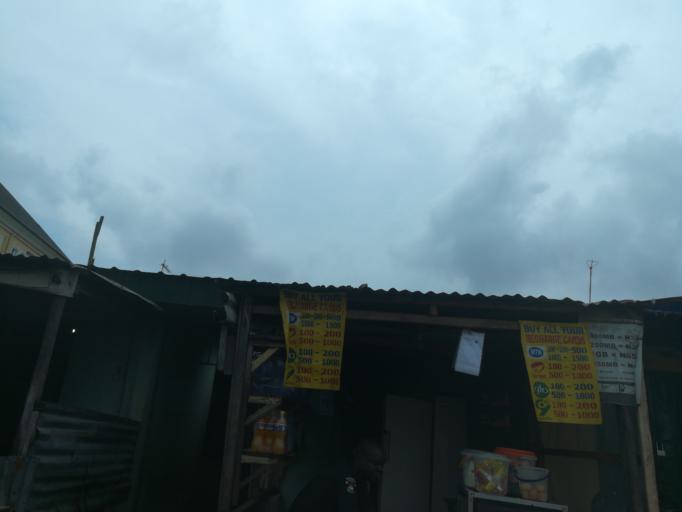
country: NG
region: Lagos
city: Oshodi
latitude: 6.5617
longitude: 3.3471
